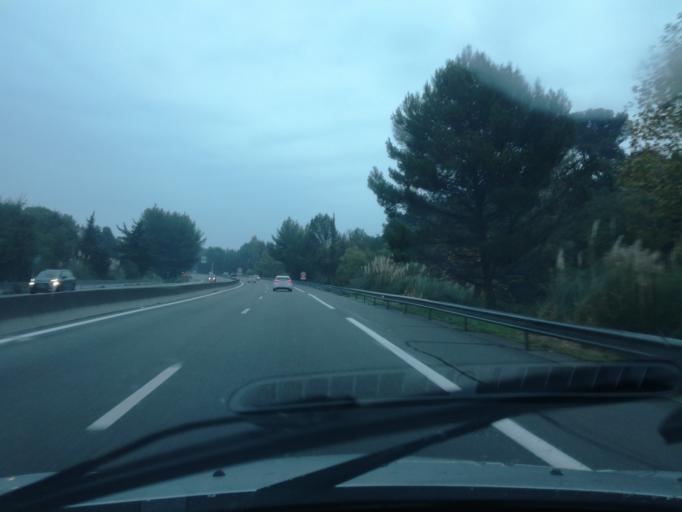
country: FR
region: Provence-Alpes-Cote d'Azur
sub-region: Departement des Alpes-Maritimes
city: Mougins
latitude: 43.5982
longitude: 7.0017
